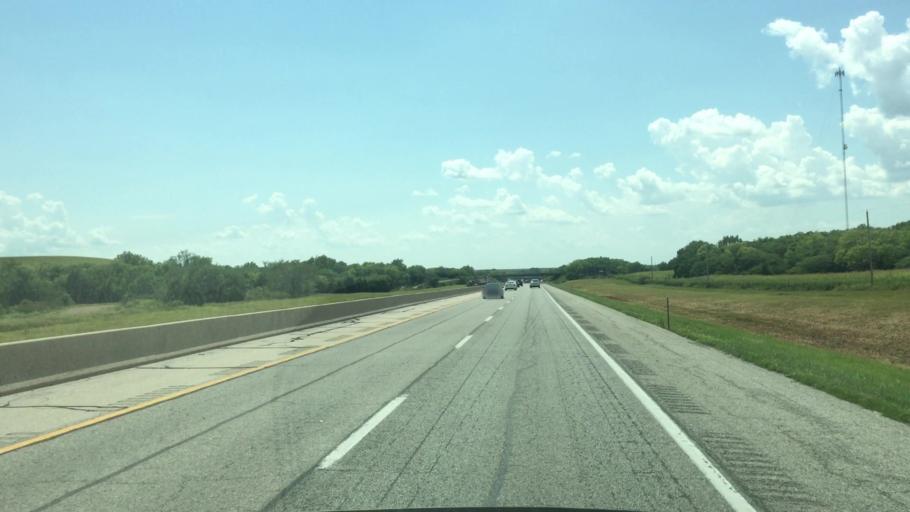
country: US
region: Kansas
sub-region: Chase County
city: Cottonwood Falls
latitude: 38.1474
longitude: -96.5058
